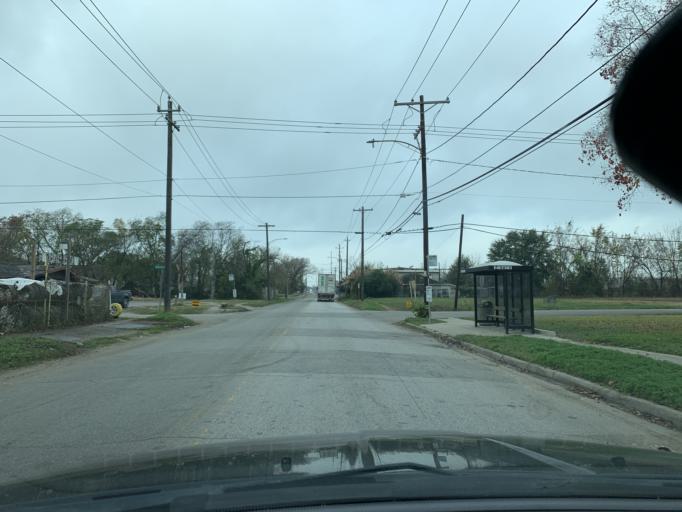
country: US
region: Texas
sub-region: Harris County
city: Houston
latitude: 29.7835
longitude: -95.3436
